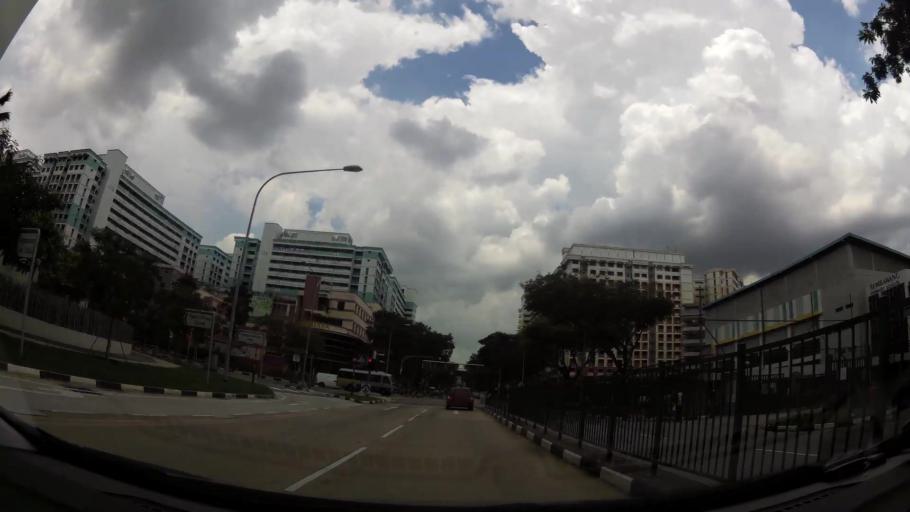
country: MY
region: Johor
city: Kampung Pasir Gudang Baru
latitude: 1.4445
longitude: 103.8203
